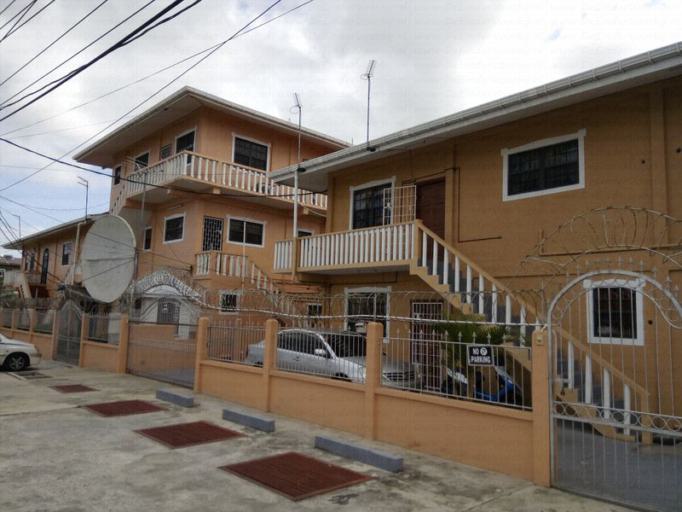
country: GY
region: Demerara-Mahaica
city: Georgetown
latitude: 6.8125
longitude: -58.1329
